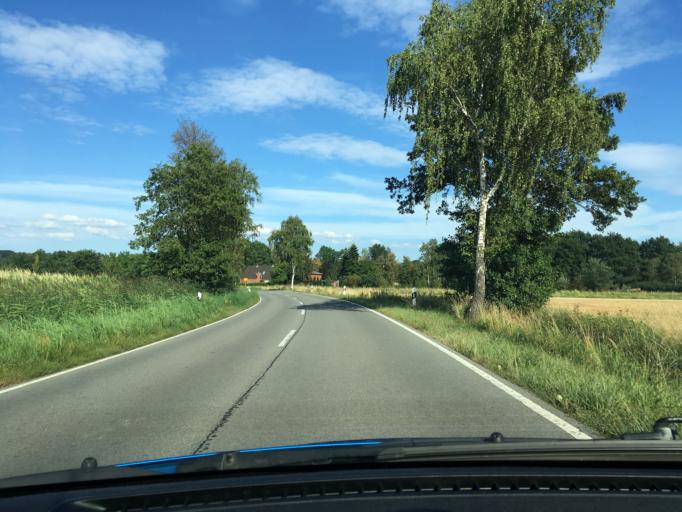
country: DE
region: Lower Saxony
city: Tespe
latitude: 53.3875
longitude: 10.4362
